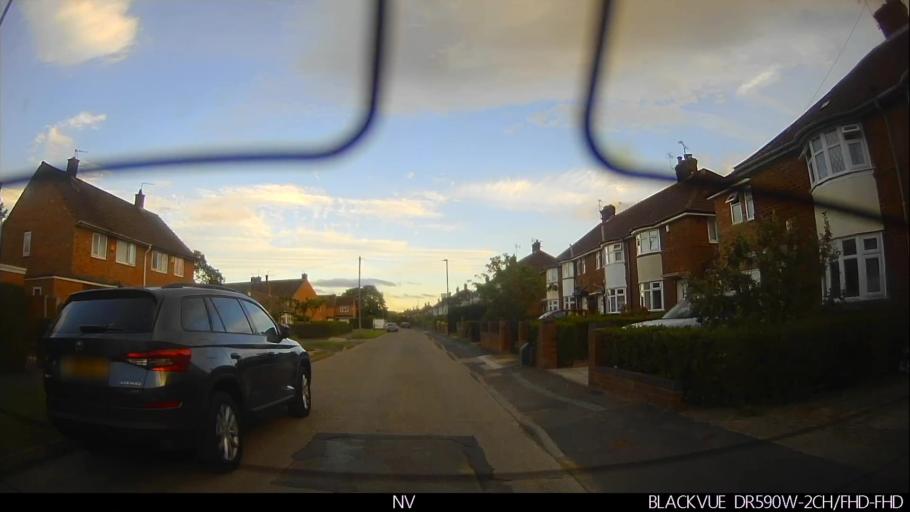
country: GB
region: England
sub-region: City of York
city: Bishopthorpe
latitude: 53.9485
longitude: -1.1219
